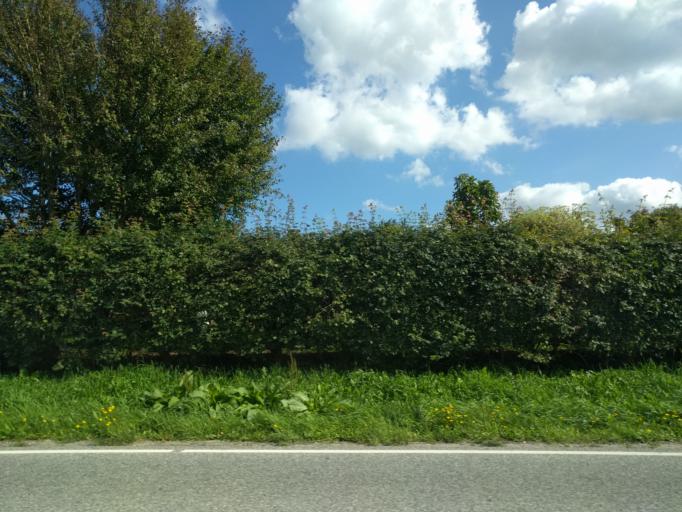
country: DK
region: Central Jutland
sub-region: Skive Kommune
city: Skive
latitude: 56.5882
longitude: 9.0294
